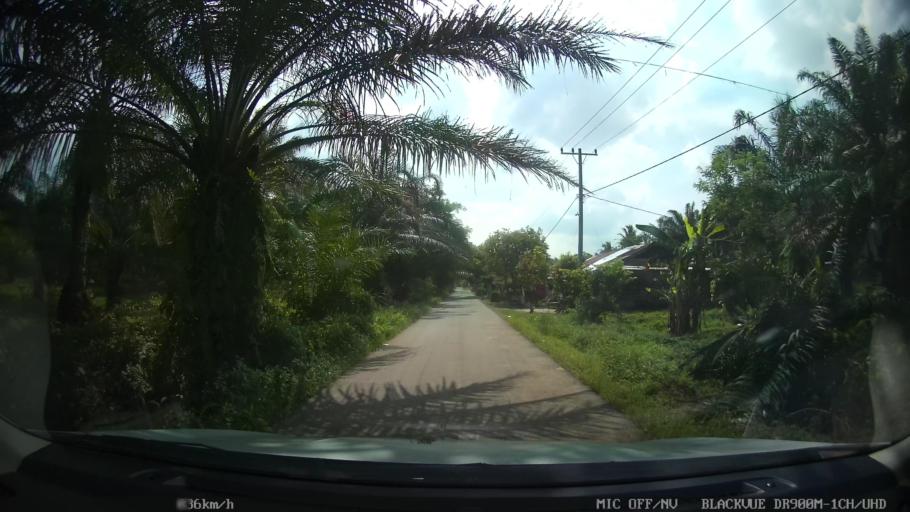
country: ID
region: North Sumatra
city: Binjai
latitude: 3.6345
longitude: 98.5256
